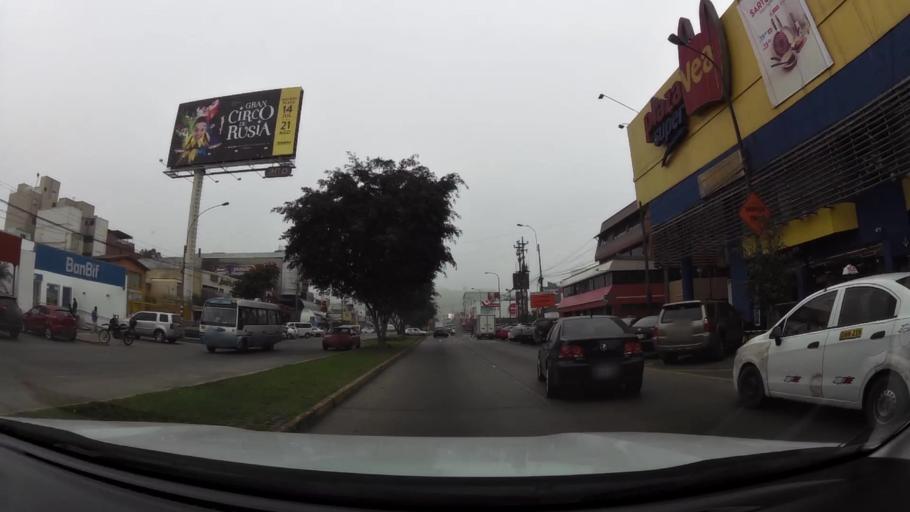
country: PE
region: Lima
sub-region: Lima
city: Surco
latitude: -12.1292
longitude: -76.9836
